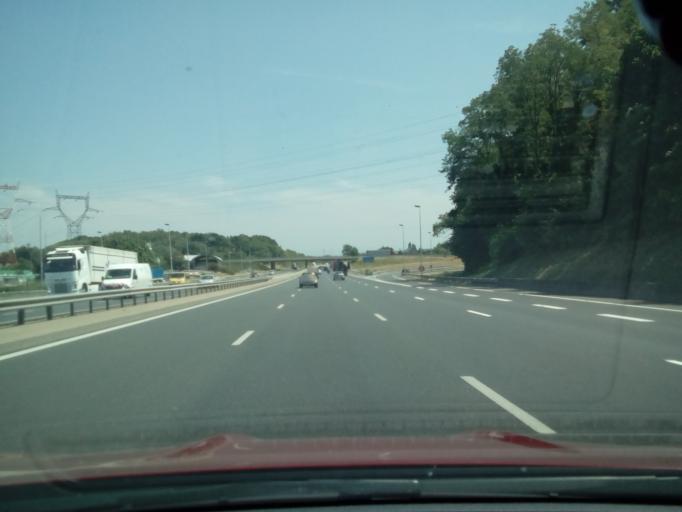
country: FR
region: Rhone-Alpes
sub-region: Departement de l'Isere
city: Grenay
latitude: 45.6545
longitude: 5.0946
